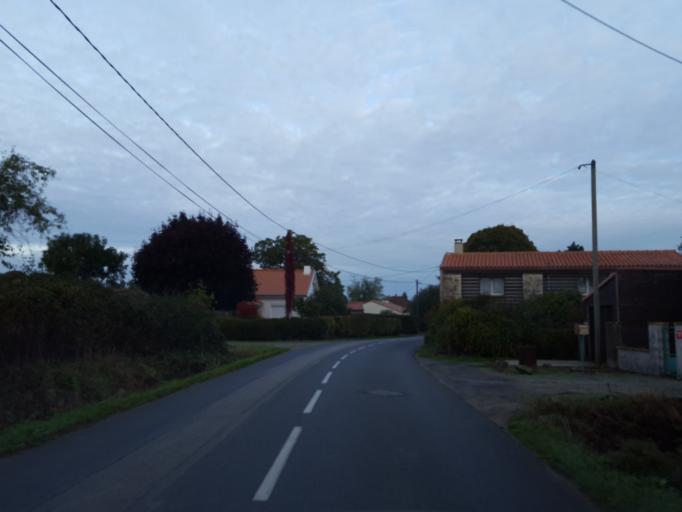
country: FR
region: Pays de la Loire
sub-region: Departement de la Loire-Atlantique
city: Saint-Julien-de-Concelles
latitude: 47.2435
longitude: -1.3946
